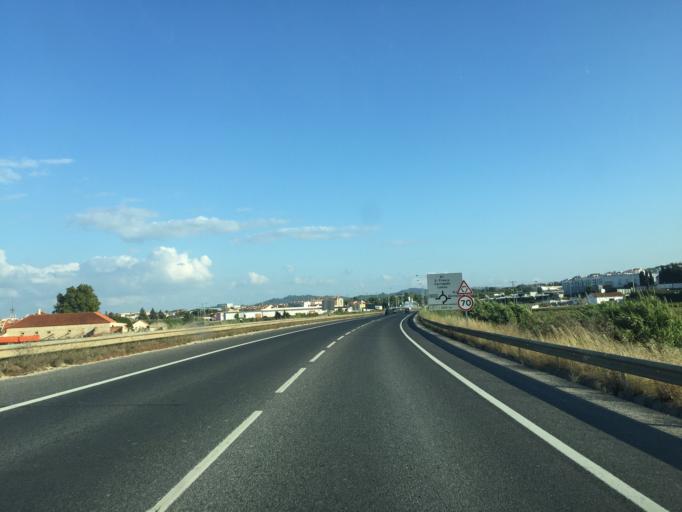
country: PT
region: Lisbon
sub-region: Alenquer
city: Alenquer
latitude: 39.0530
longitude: -8.9943
